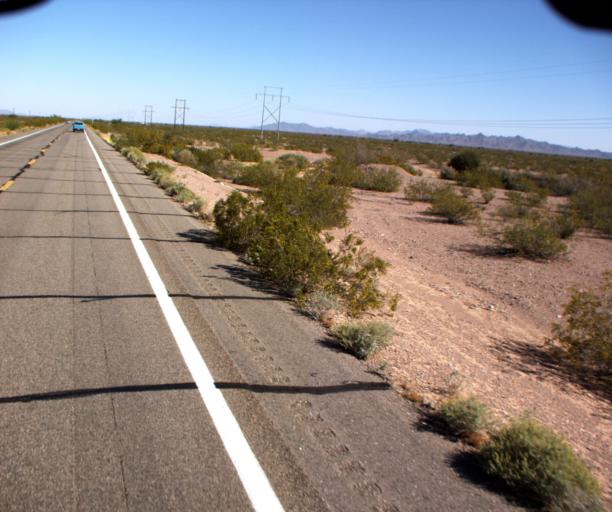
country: US
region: Arizona
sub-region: La Paz County
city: Quartzsite
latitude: 33.3811
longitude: -114.2171
